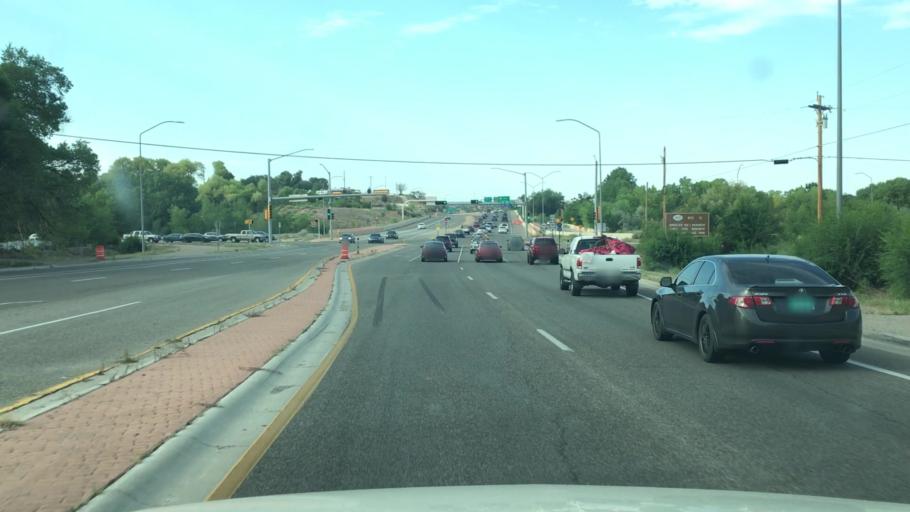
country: US
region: New Mexico
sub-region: Santa Fe County
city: Pojoaque
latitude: 35.8985
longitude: -106.0208
